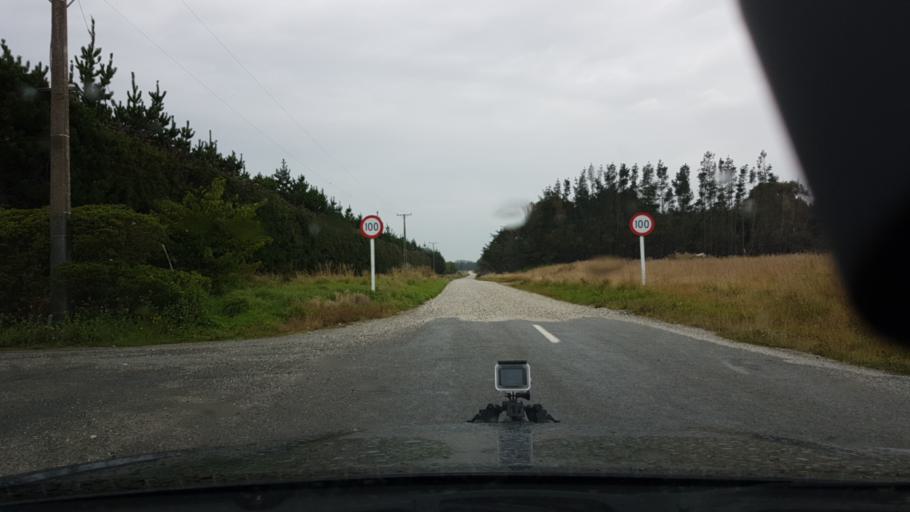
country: NZ
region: Southland
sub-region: Invercargill City
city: Invercargill
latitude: -46.4681
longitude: 168.3898
